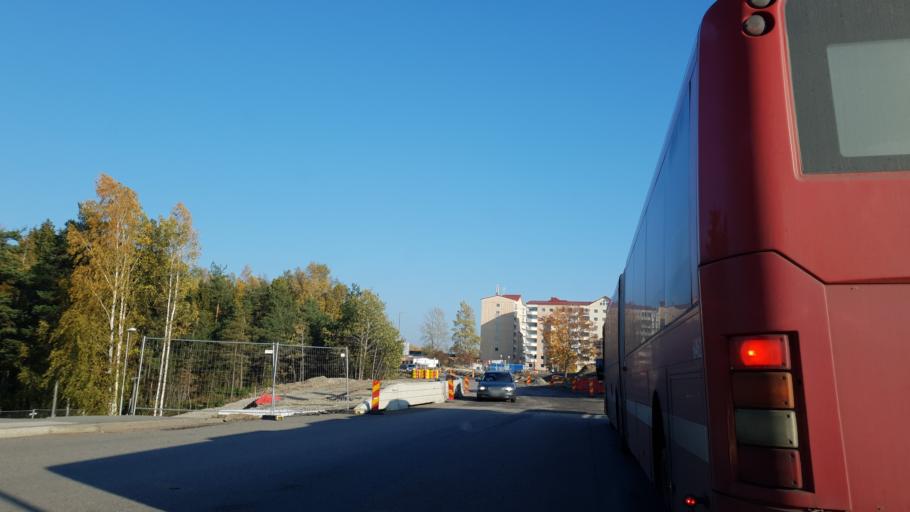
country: SE
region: Stockholm
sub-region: Haninge Kommun
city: Haninge
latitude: 59.1729
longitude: 18.1692
